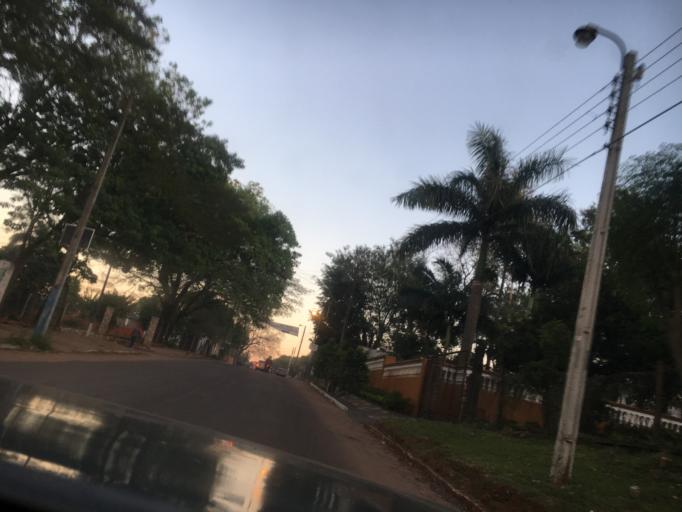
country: PY
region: Central
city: Villa Elisa
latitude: -25.3606
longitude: -57.5842
